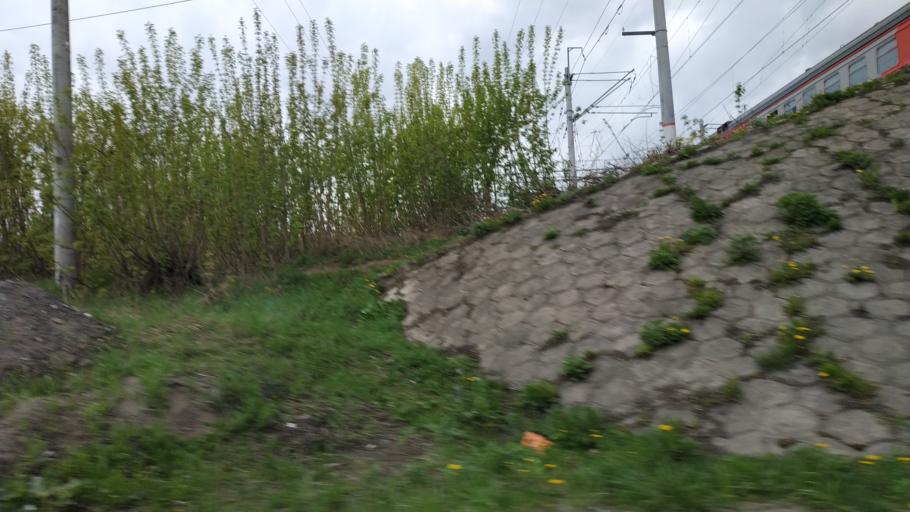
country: RU
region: Moskovskaya
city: Pavlovskiy Posad
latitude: 55.7748
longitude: 38.6863
